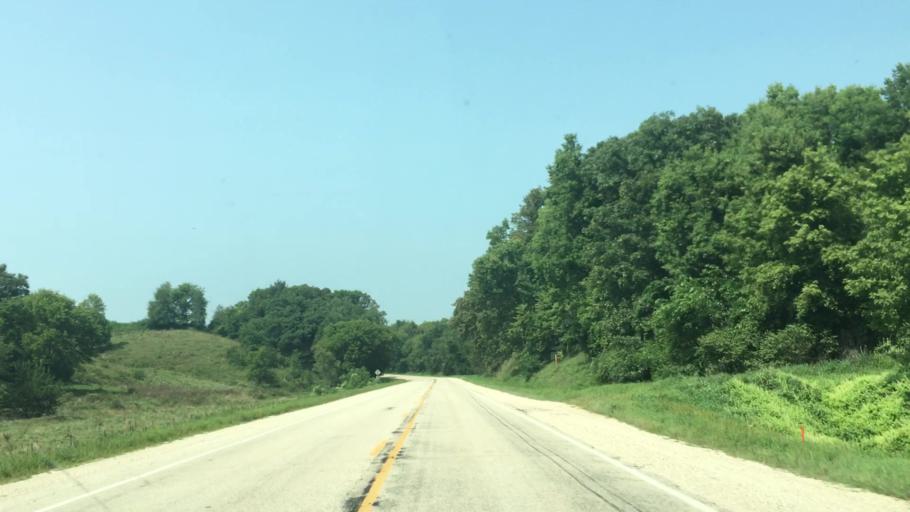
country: US
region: Iowa
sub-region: Fayette County
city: West Union
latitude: 43.0749
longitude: -91.8392
